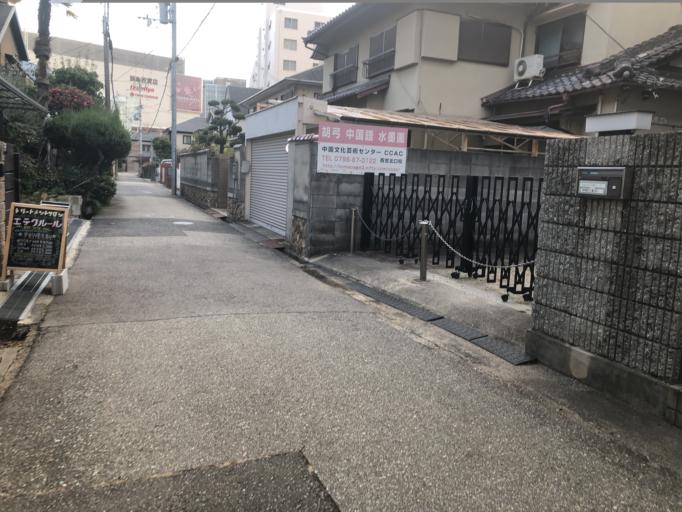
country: JP
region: Hyogo
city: Nishinomiya-hama
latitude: 34.7455
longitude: 135.3582
